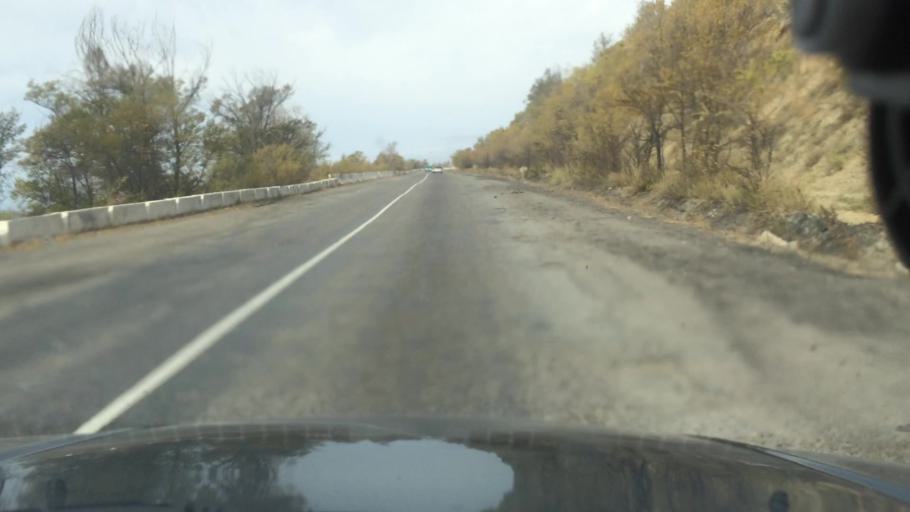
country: KG
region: Ysyk-Koel
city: Karakol
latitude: 42.5960
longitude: 78.3804
